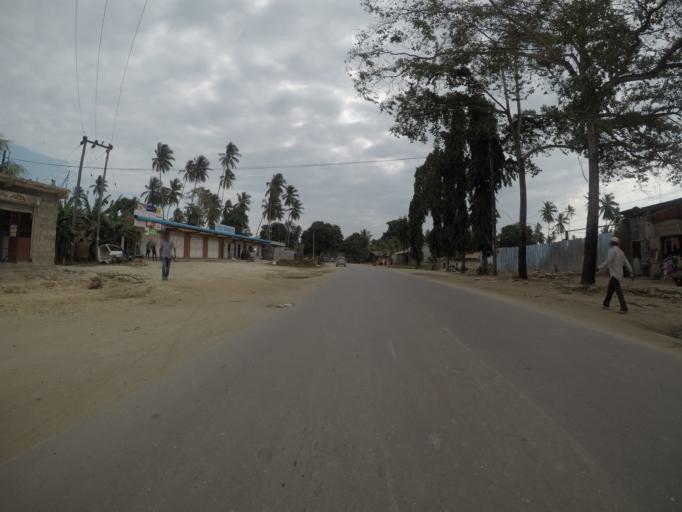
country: TZ
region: Zanzibar Central/South
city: Koani
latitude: -6.1955
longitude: 39.2680
